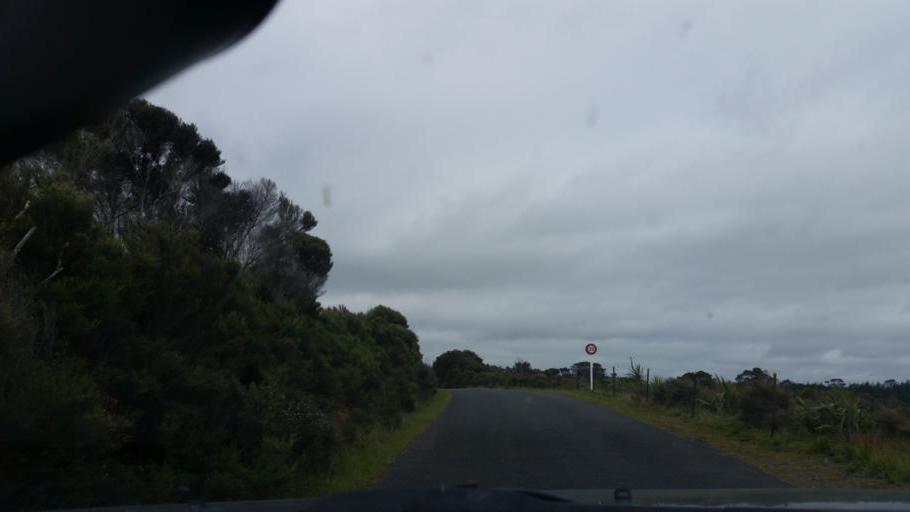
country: NZ
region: Northland
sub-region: Kaipara District
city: Dargaville
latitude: -35.8126
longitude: 173.6503
